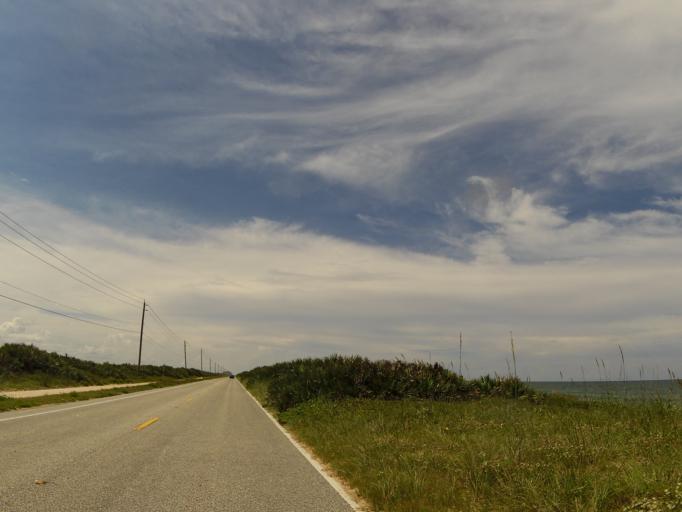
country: US
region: Florida
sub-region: Volusia County
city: Ormond-by-the-Sea
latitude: 29.4001
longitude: -81.0904
